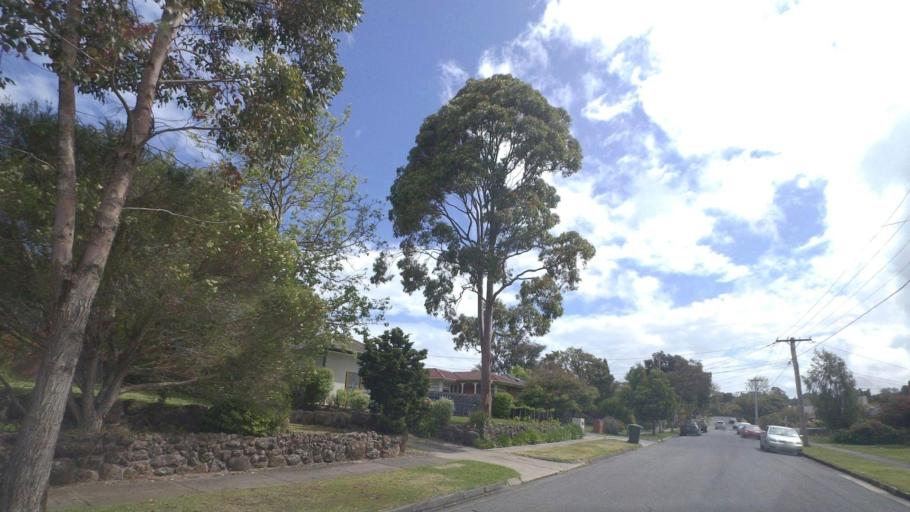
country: AU
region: Victoria
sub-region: Whitehorse
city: Vermont
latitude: -37.8347
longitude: 145.2086
